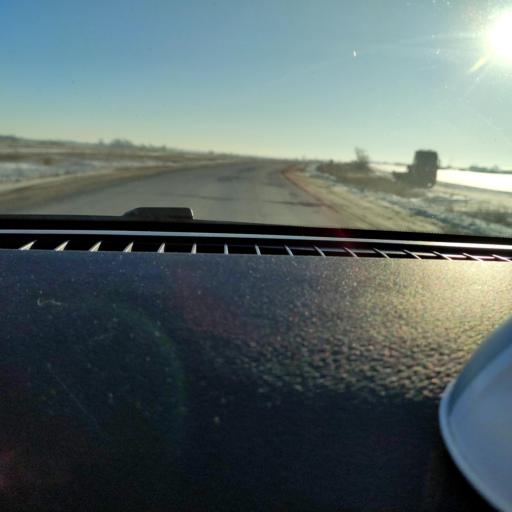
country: RU
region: Samara
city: Spiridonovka
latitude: 53.1406
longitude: 50.5986
